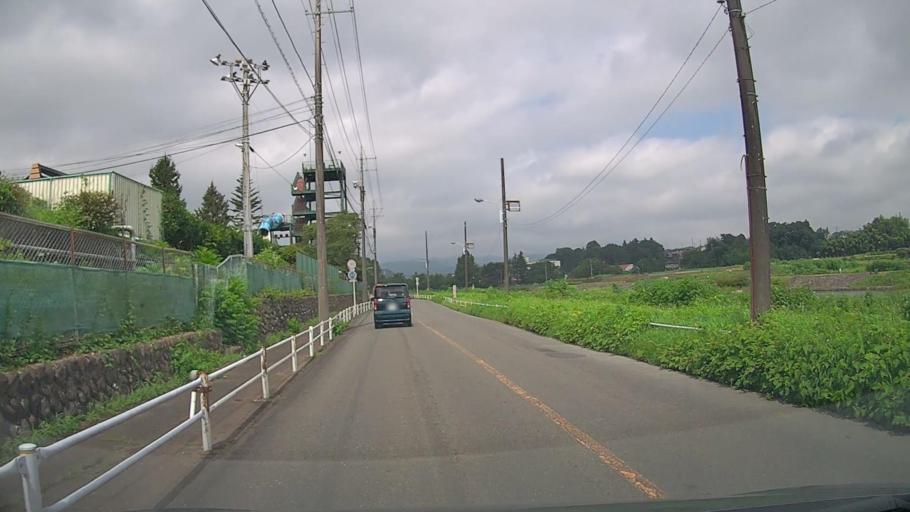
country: JP
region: Tokyo
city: Fussa
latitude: 35.7182
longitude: 139.2765
